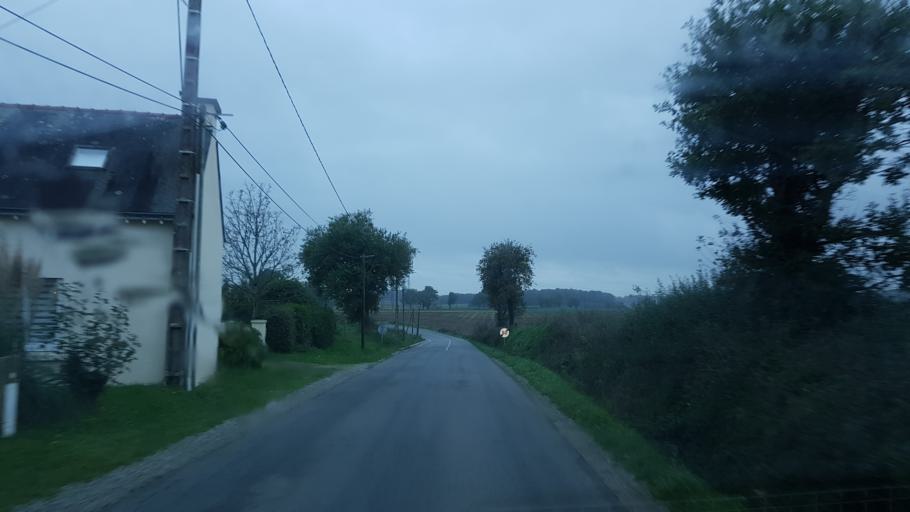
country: FR
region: Brittany
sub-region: Departement du Morbihan
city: Trefflean
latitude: 47.6604
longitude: -2.6245
